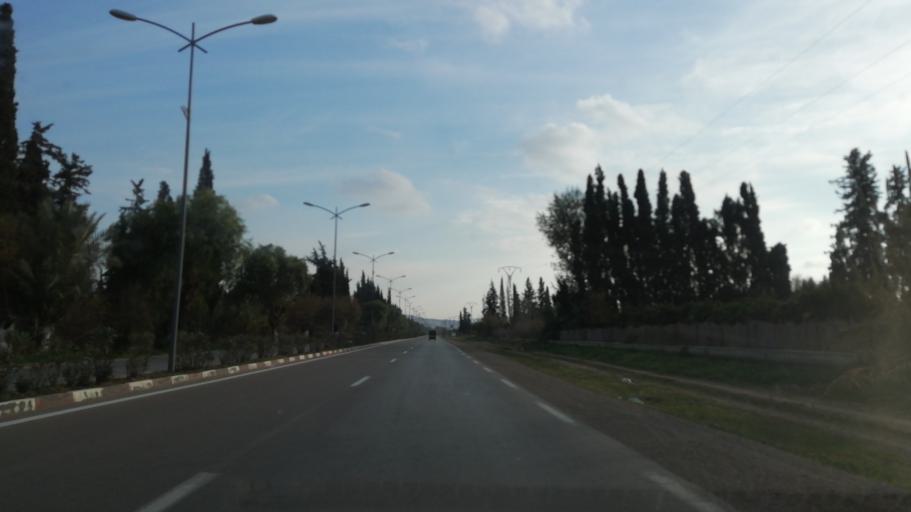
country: DZ
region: Mascara
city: Mascara
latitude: 35.6087
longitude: 0.0631
